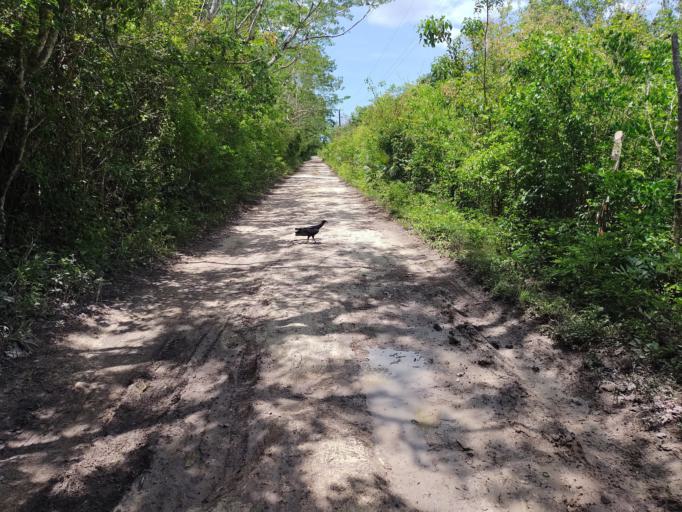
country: MX
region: Quintana Roo
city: San Miguel de Cozumel
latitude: 20.4992
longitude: -86.9016
